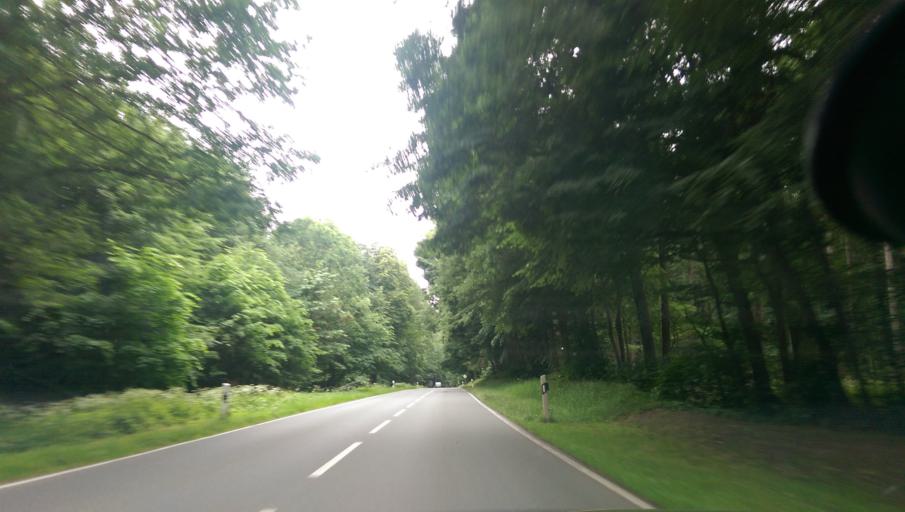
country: DE
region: Lower Saxony
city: Bomlitz
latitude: 52.9561
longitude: 9.6537
